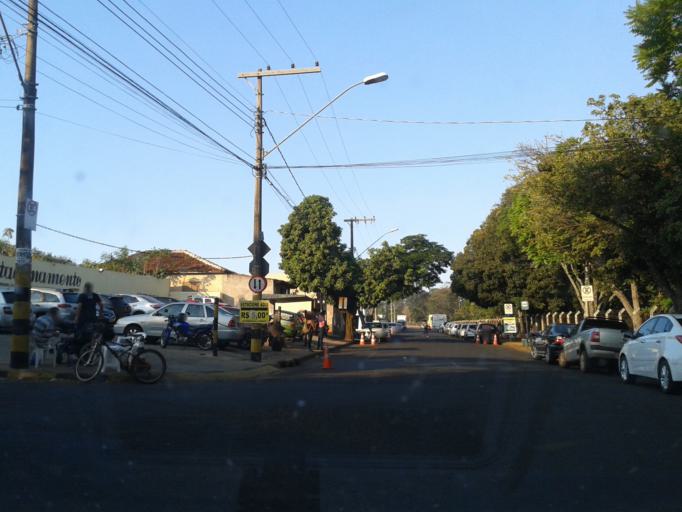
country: BR
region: Minas Gerais
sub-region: Uberlandia
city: Uberlandia
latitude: -18.9078
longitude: -48.2412
